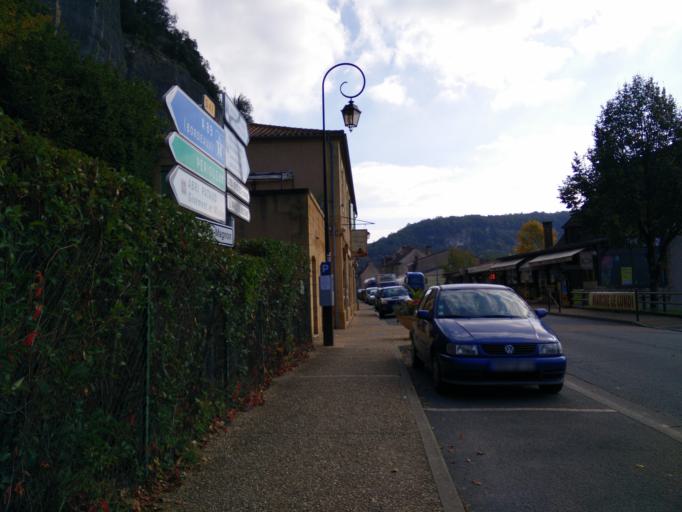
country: FR
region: Aquitaine
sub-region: Departement de la Dordogne
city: Saint-Cyprien
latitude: 44.9377
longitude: 1.0120
